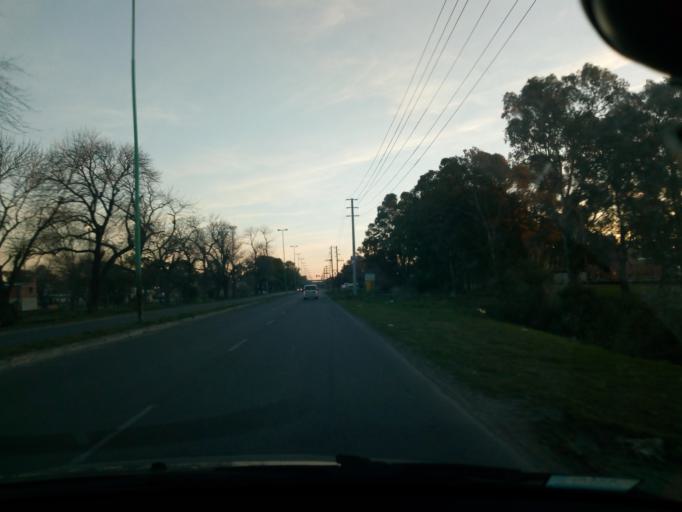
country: AR
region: Buenos Aires
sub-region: Partido de Ensenada
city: Ensenada
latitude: -34.8742
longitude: -57.9160
